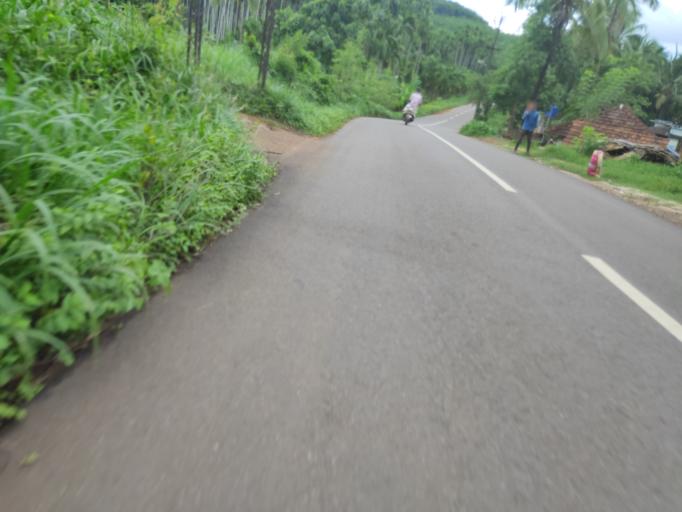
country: IN
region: Kerala
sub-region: Malappuram
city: Manjeri
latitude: 11.1704
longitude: 76.1783
